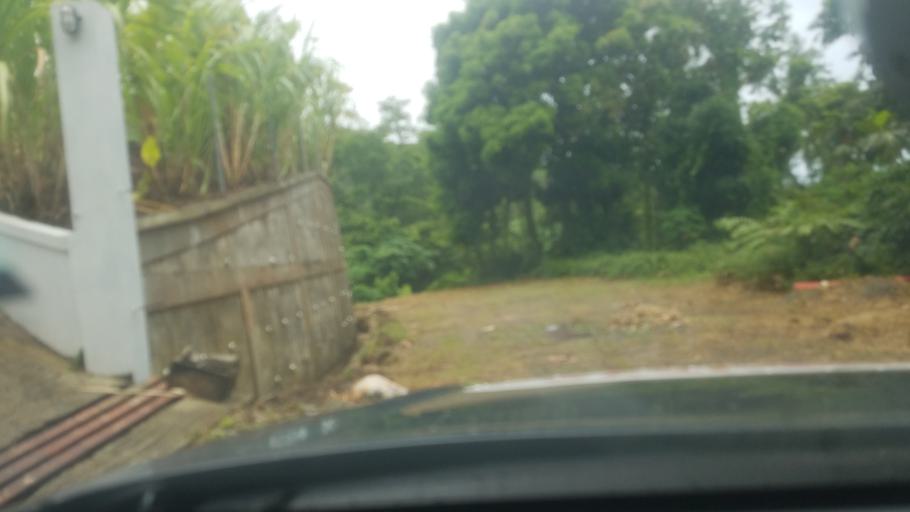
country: LC
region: Gros-Islet
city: Gros Islet
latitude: 14.0340
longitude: -60.9332
